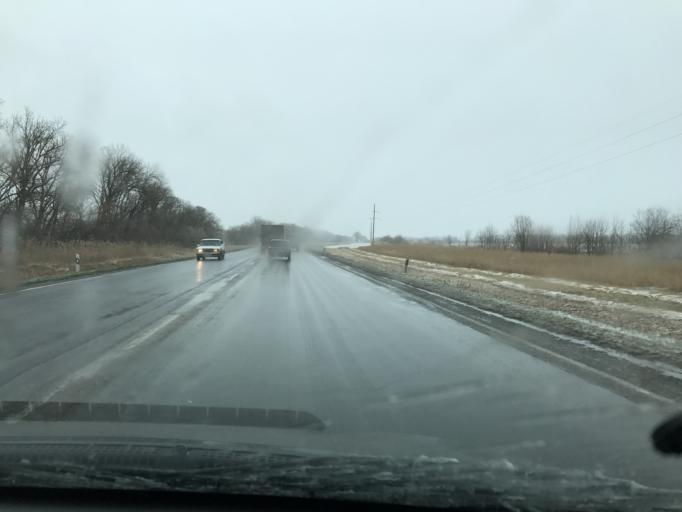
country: RU
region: Rostov
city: Zernograd
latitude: 46.8034
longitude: 40.3493
